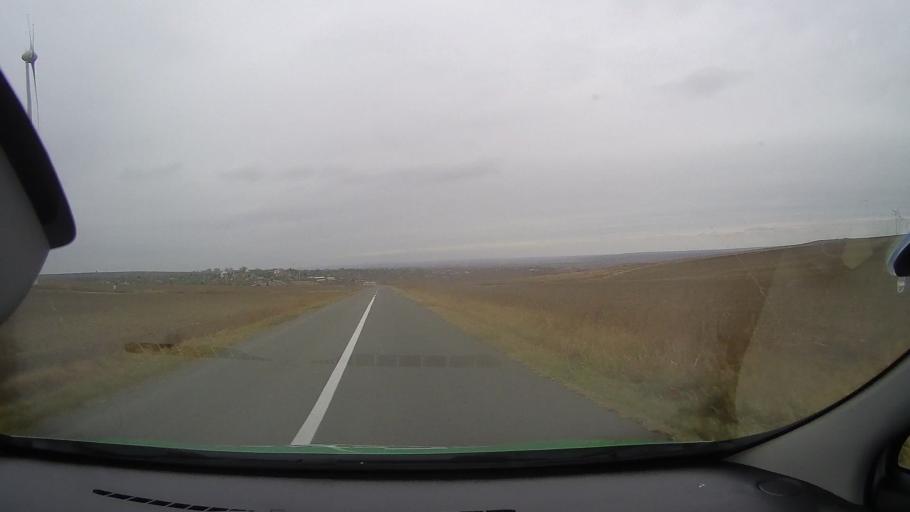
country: RO
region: Constanta
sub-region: Comuna Pantelimon
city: Pantelimon
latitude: 44.5354
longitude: 28.3267
